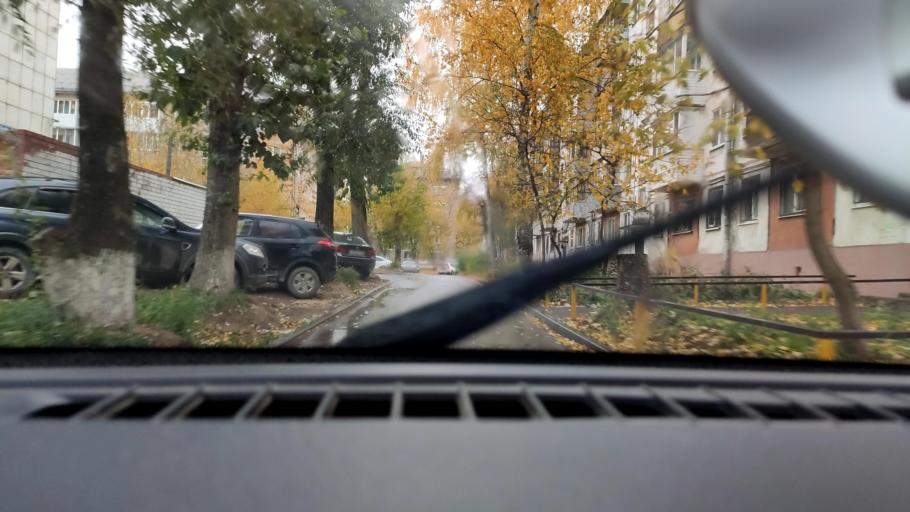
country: RU
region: Perm
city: Perm
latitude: 57.9814
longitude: 56.1906
